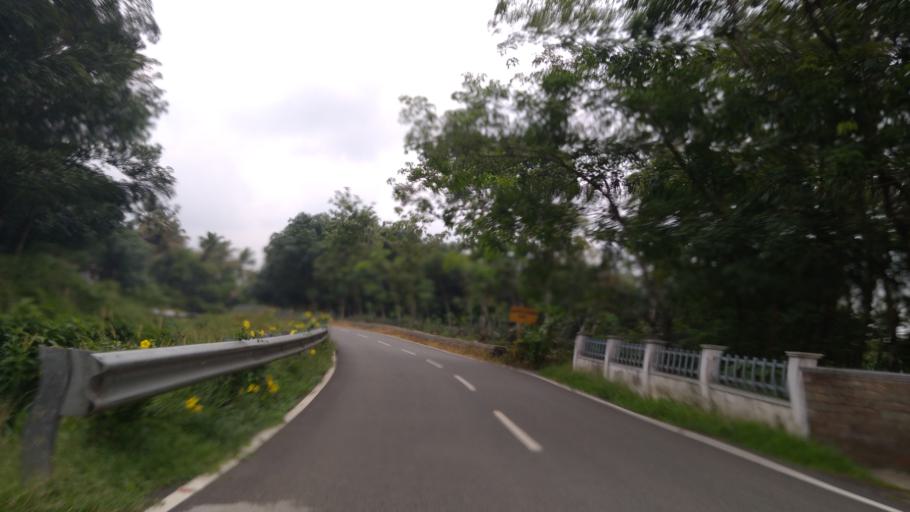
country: IN
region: Kerala
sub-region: Ernakulam
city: Ramamangalam
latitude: 10.0183
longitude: 76.4867
